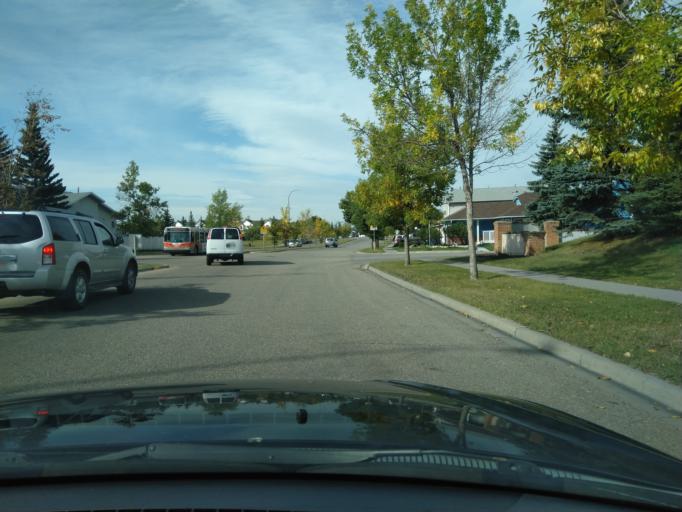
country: CA
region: Alberta
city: Calgary
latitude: 51.1350
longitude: -114.0904
